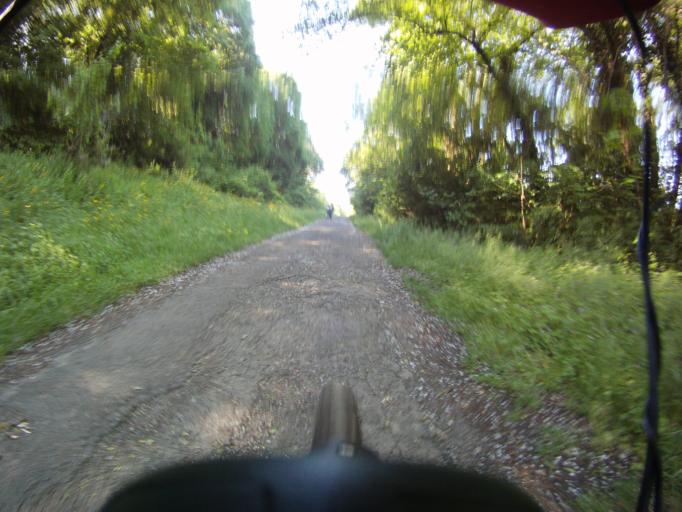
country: FR
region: Auvergne
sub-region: Departement du Puy-de-Dome
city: Mezel
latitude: 45.7603
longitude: 3.2327
